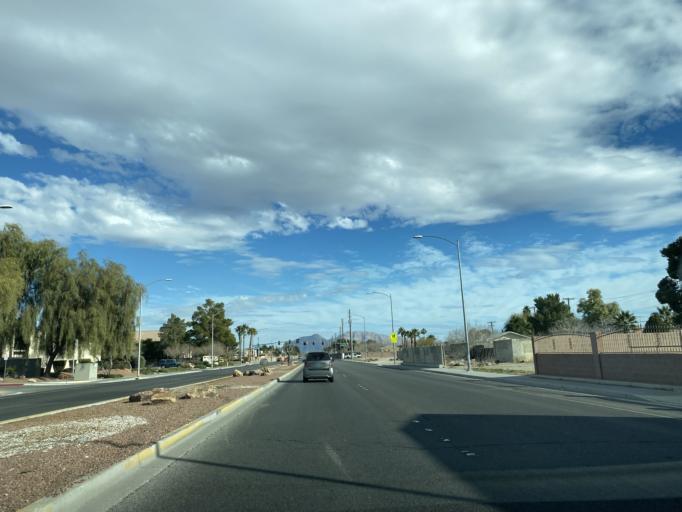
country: US
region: Nevada
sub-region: Clark County
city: Las Vegas
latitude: 36.1884
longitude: -115.1720
